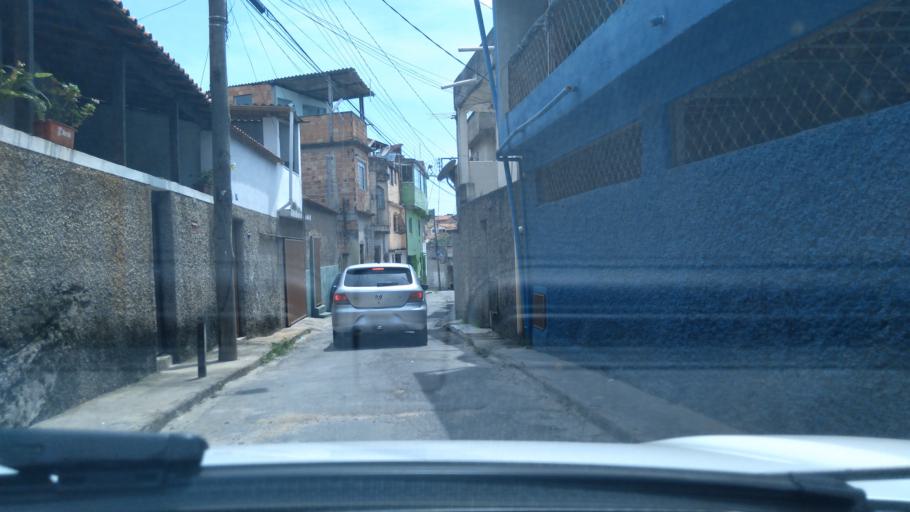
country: BR
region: Minas Gerais
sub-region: Contagem
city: Contagem
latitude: -19.9215
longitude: -44.0007
